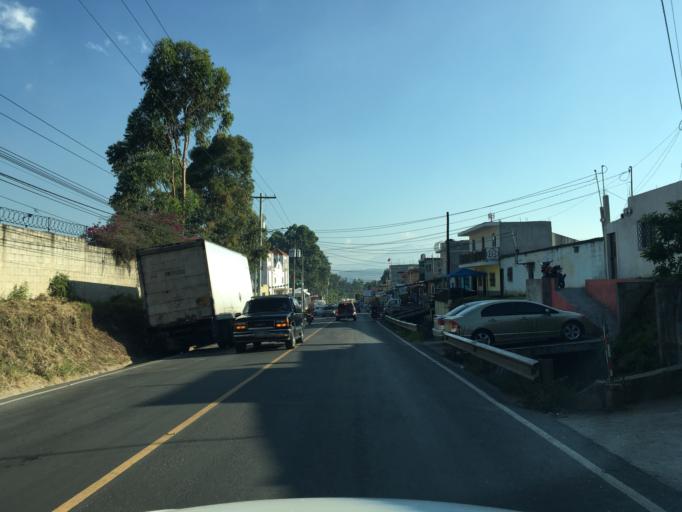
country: GT
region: Guatemala
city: Villa Nueva
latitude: 14.5421
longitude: -90.6160
